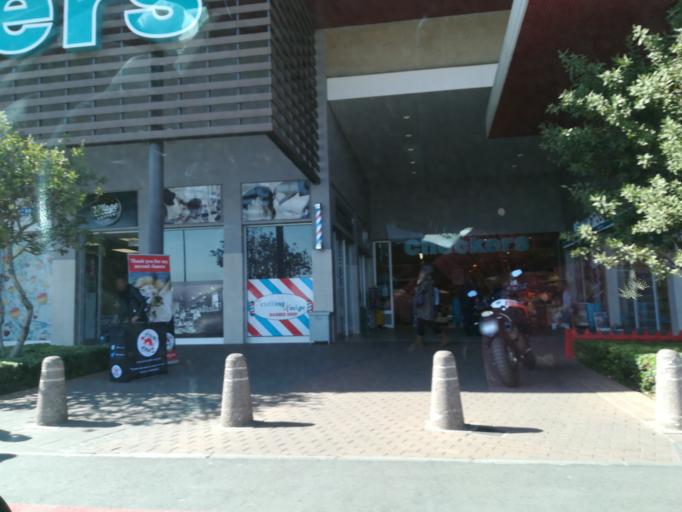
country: ZA
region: Gauteng
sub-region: City of Tshwane Metropolitan Municipality
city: Pretoria
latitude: -25.7995
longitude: 28.3333
